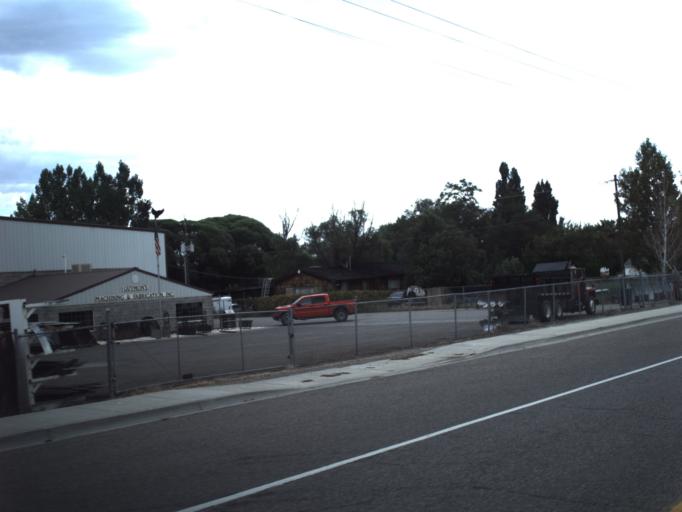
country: US
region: Utah
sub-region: Emery County
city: Huntington
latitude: 39.3525
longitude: -110.8520
